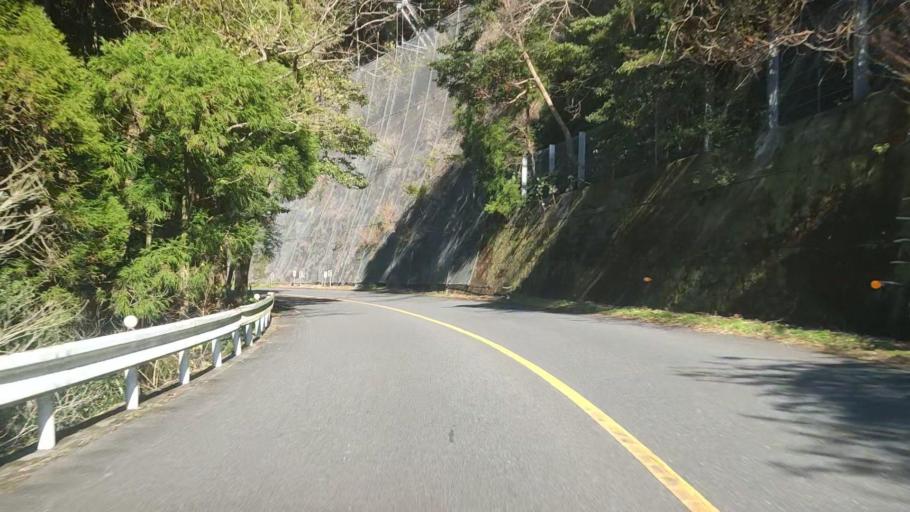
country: JP
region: Oita
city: Saiki
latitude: 32.8788
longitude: 131.9489
